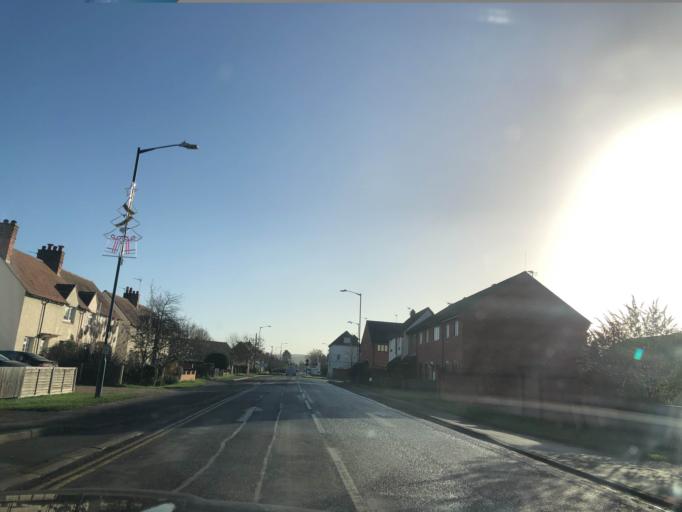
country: GB
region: England
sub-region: Warwickshire
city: Wellesbourne Mountford
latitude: 52.1973
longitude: -1.5930
